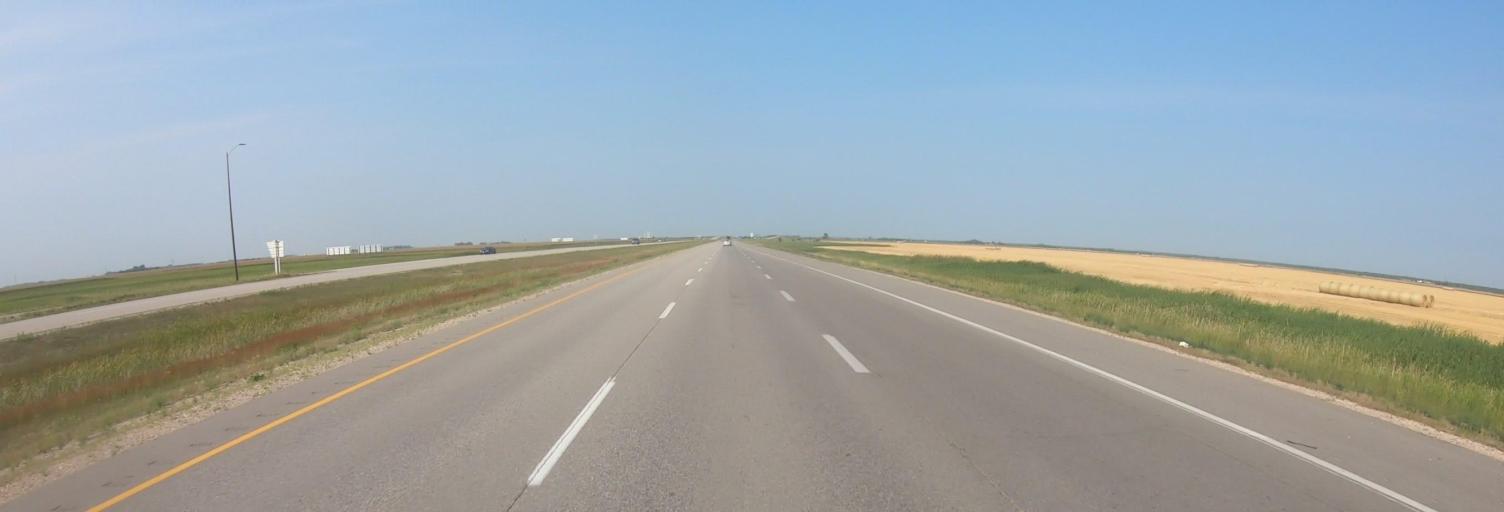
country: CA
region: Manitoba
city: Steinbach
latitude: 49.6835
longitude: -96.6592
